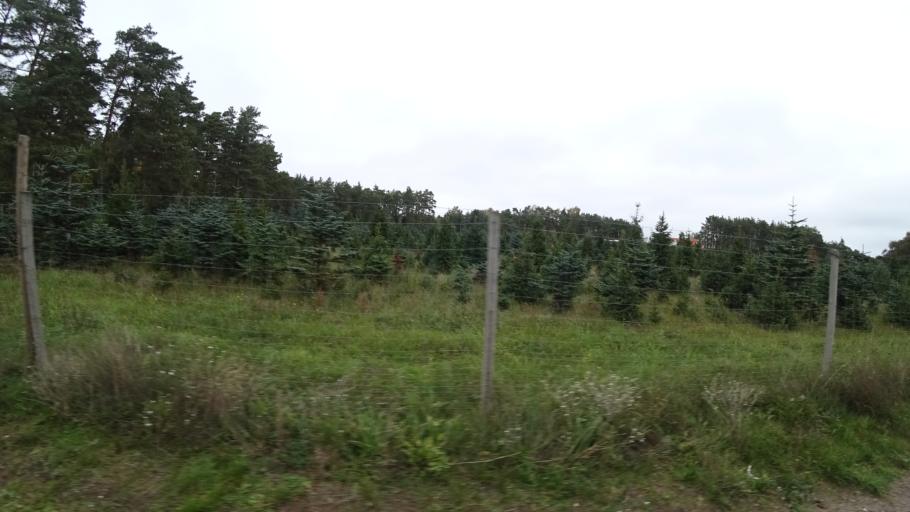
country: SE
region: Skane
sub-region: Kavlinge Kommun
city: Hofterup
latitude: 55.8207
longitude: 12.9683
